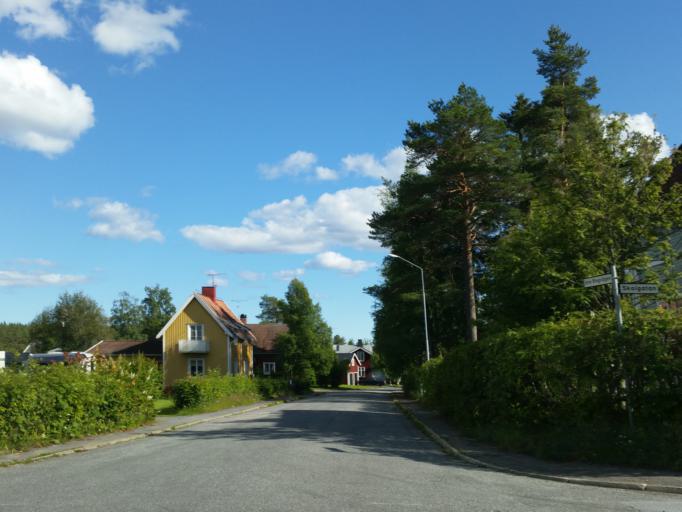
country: SE
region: Vaesterbotten
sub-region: Robertsfors Kommun
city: Robertsfors
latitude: 64.1929
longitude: 20.8572
